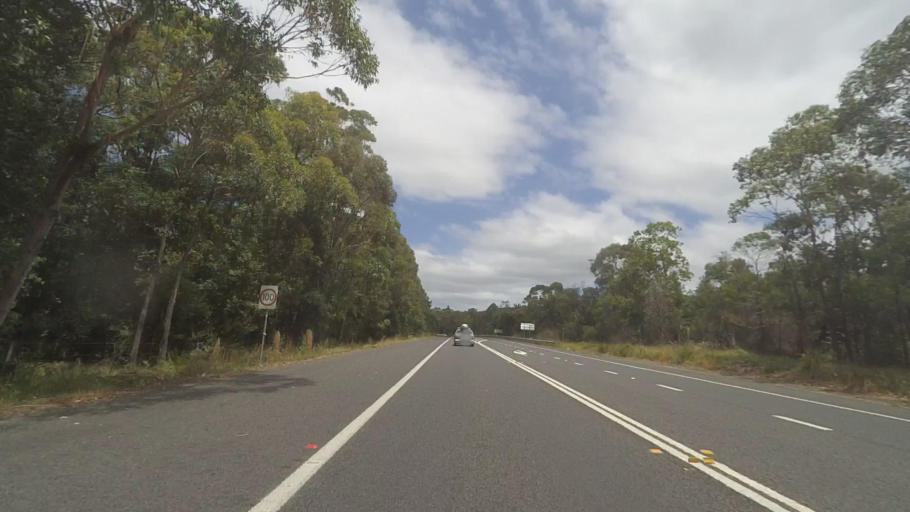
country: AU
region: New South Wales
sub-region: Shoalhaven Shire
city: Milton
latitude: -35.2317
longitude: 150.4330
